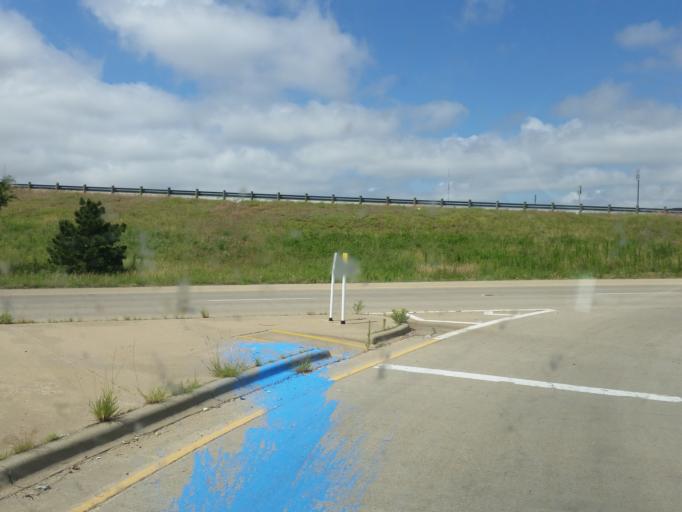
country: US
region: Texas
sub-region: Lubbock County
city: Lubbock
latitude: 33.5393
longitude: -101.8457
